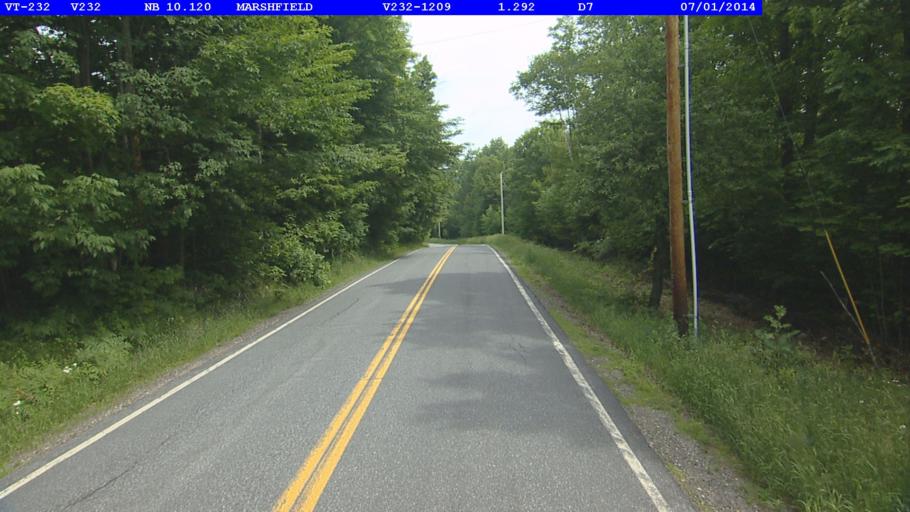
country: US
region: Vermont
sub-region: Caledonia County
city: Hardwick
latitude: 44.3322
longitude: -72.2815
